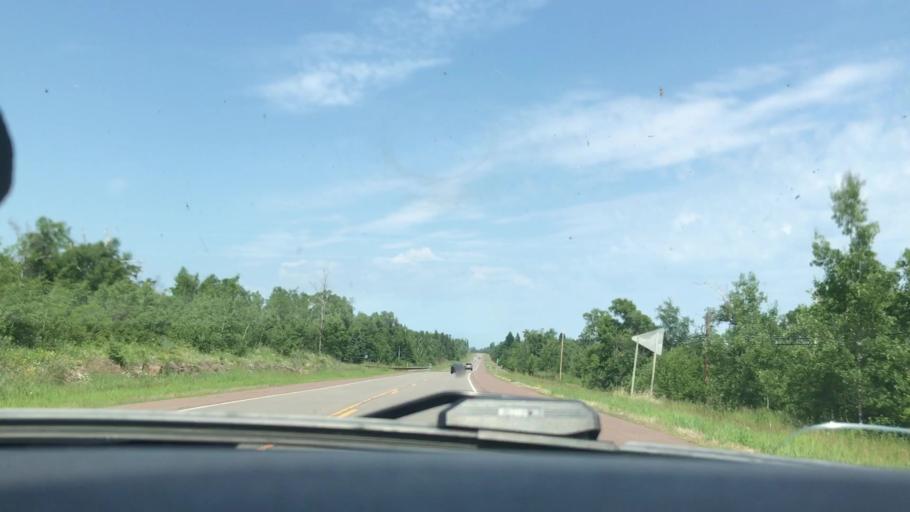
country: US
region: Minnesota
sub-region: Cook County
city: Grand Marais
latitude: 47.5859
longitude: -90.8138
